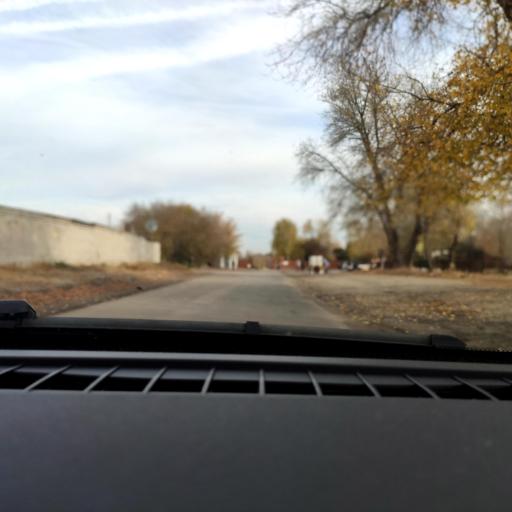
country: RU
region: Voronezj
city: Voronezh
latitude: 51.6617
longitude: 39.2896
